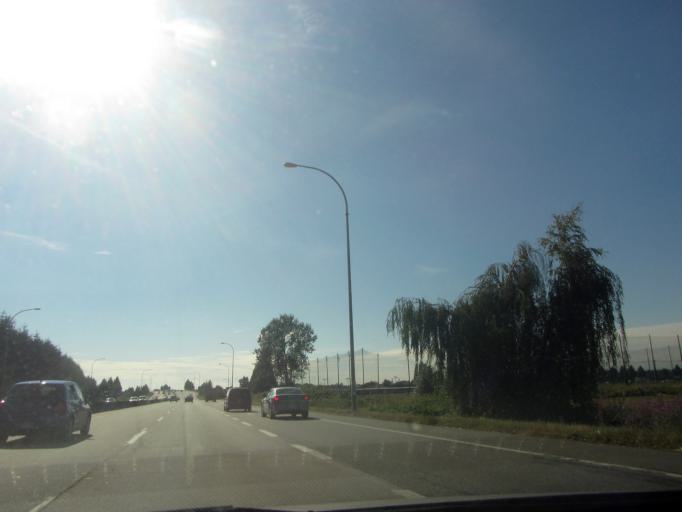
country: CA
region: British Columbia
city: Richmond
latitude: 49.1779
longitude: -123.0627
